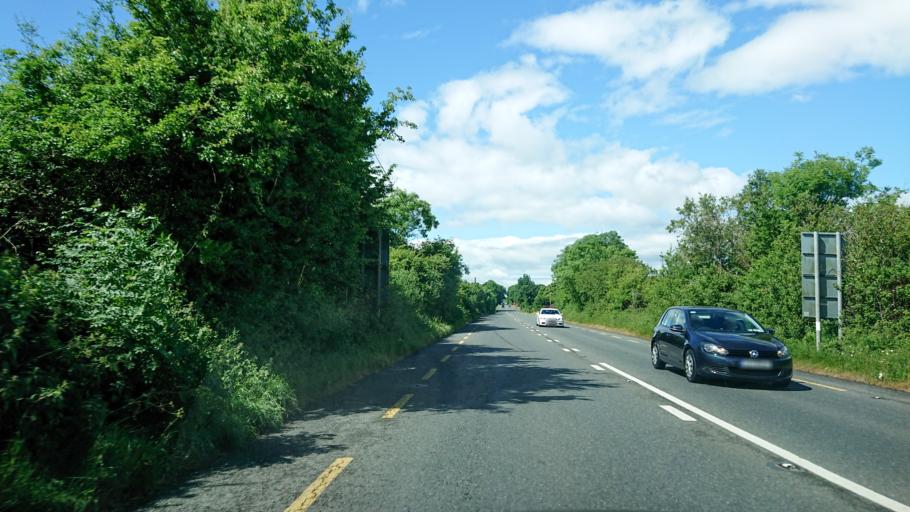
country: IE
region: Munster
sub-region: Waterford
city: Waterford
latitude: 52.2376
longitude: -7.1805
